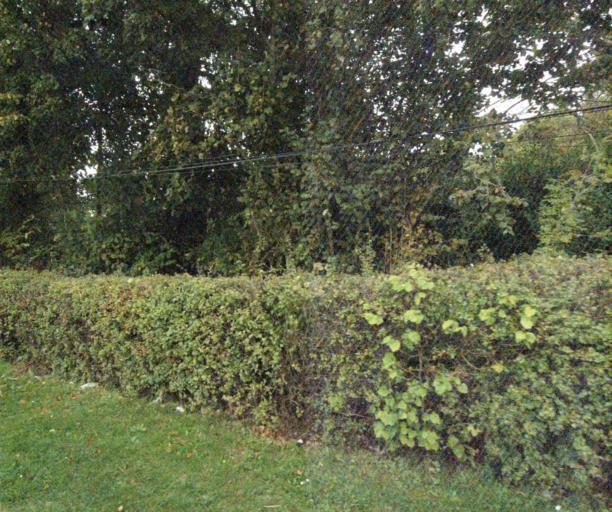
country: FR
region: Nord-Pas-de-Calais
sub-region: Departement du Nord
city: Marquillies
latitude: 50.5613
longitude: 2.8682
